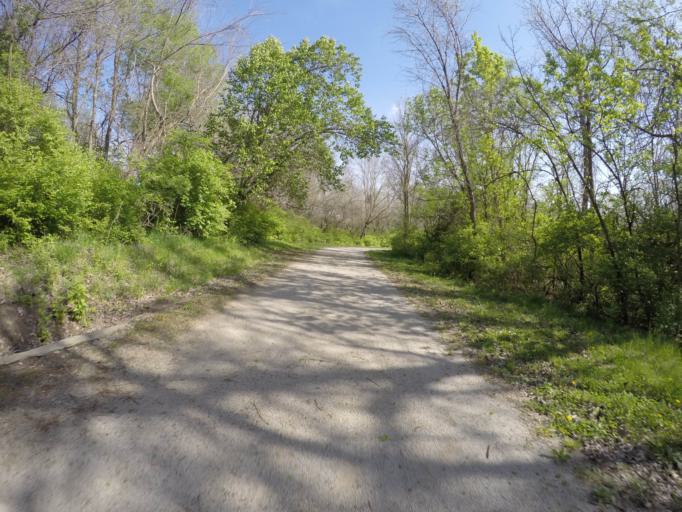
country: US
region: Missouri
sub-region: Jackson County
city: Grandview
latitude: 38.9009
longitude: -94.4888
